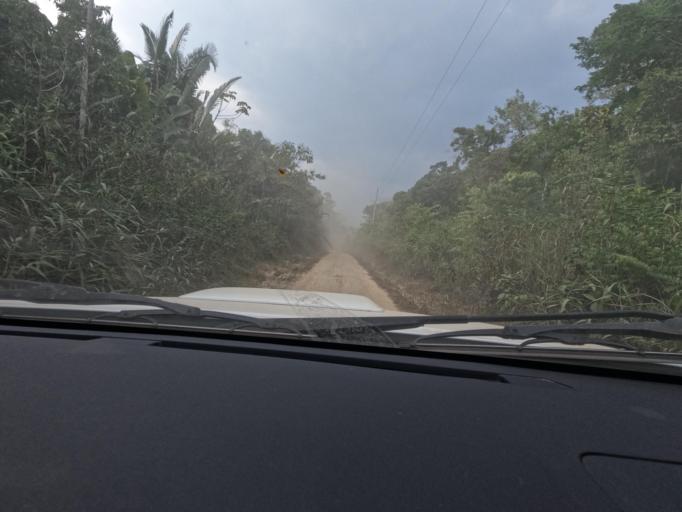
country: BR
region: Rondonia
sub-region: Porto Velho
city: Porto Velho
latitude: -8.5691
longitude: -64.0228
